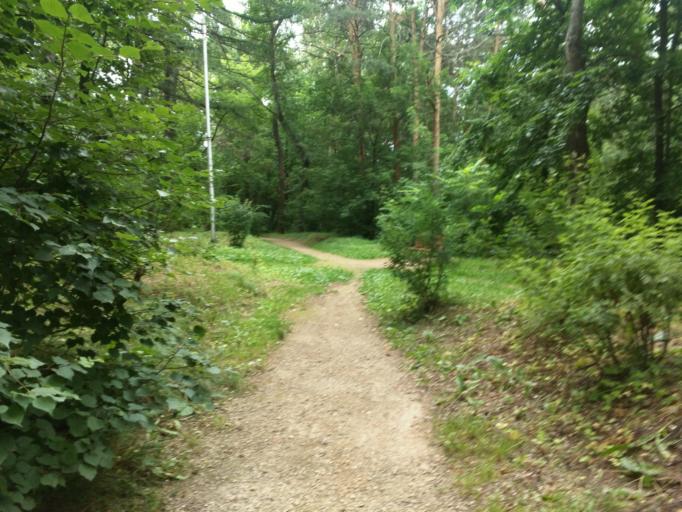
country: RU
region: Tatarstan
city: Yelabuga
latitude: 55.7561
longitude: 52.0473
